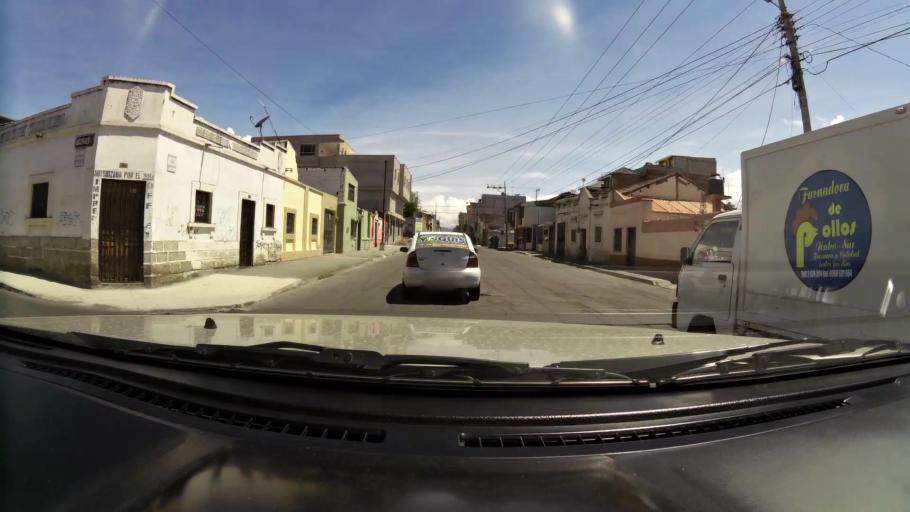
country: EC
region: Chimborazo
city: Riobamba
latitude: -1.6776
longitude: -78.6509
